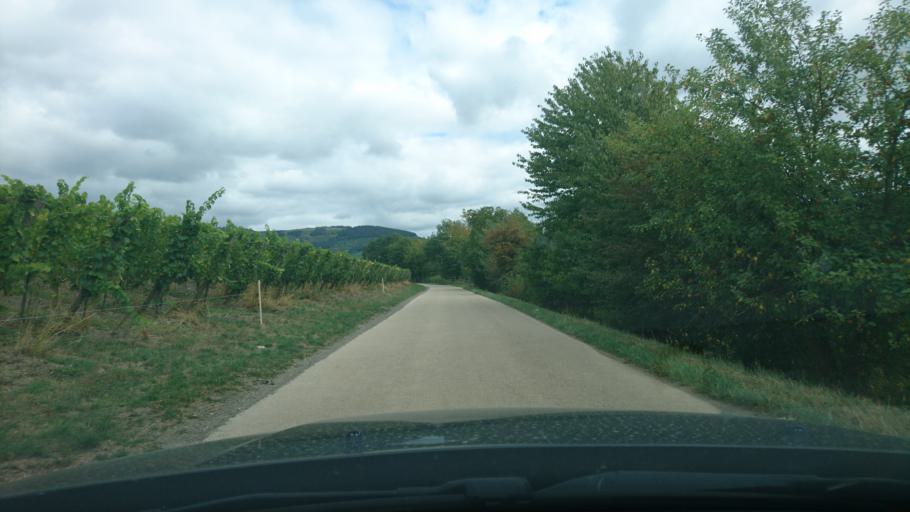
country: DE
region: Rheinland-Pfalz
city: Wiltingen
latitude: 49.6621
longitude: 6.6198
